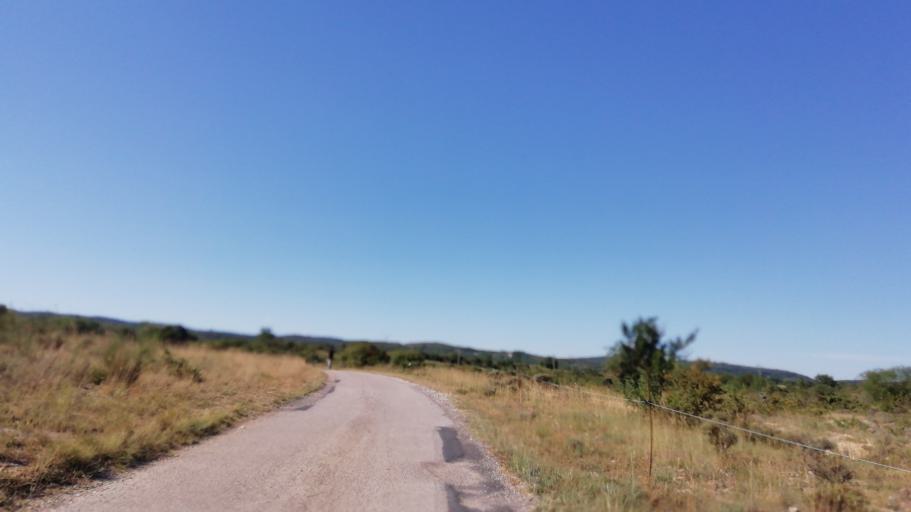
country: FR
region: Languedoc-Roussillon
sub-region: Departement de l'Herault
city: Saint-Martin-de-Londres
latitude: 43.7997
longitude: 3.7600
